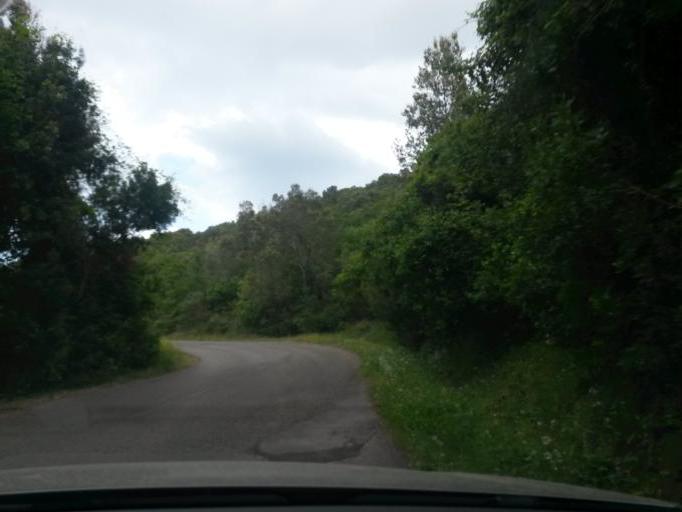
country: IT
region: Tuscany
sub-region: Provincia di Livorno
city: Rio nell'Elba
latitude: 42.8258
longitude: 10.3958
